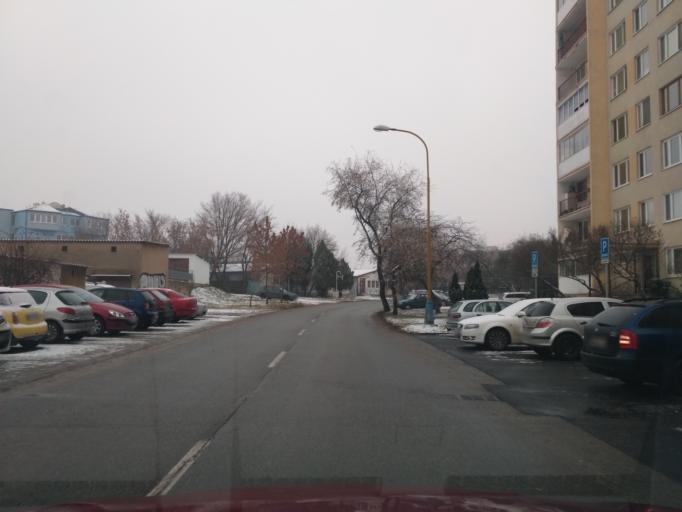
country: SK
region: Kosicky
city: Kosice
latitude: 48.7043
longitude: 21.2341
